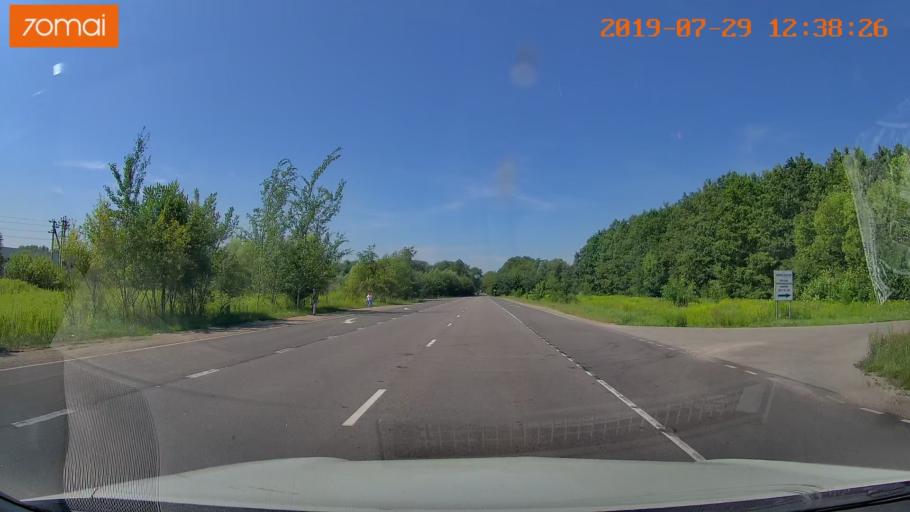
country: RU
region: Kaliningrad
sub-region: Gorod Kaliningrad
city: Kaliningrad
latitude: 54.6584
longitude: 20.5520
